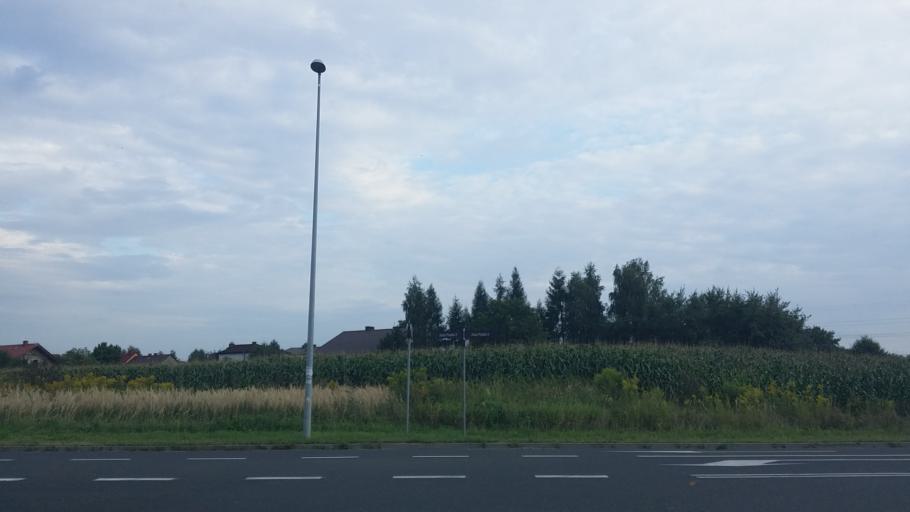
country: PL
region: Lesser Poland Voivodeship
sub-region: Powiat oswiecimski
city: Zator
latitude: 49.9925
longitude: 19.4269
